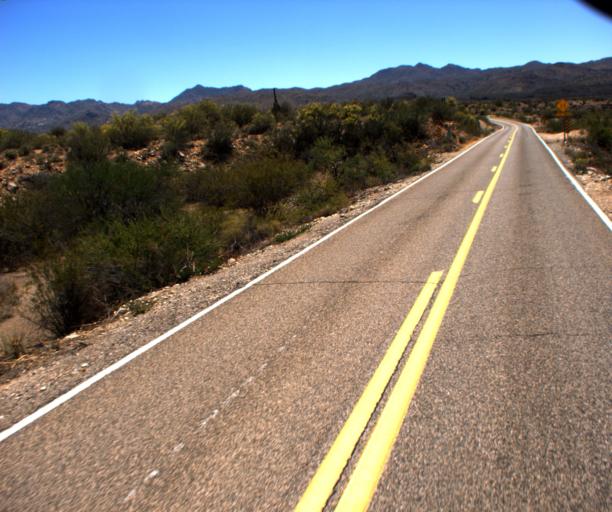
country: US
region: Arizona
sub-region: Yavapai County
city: Bagdad
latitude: 34.4873
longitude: -113.0646
